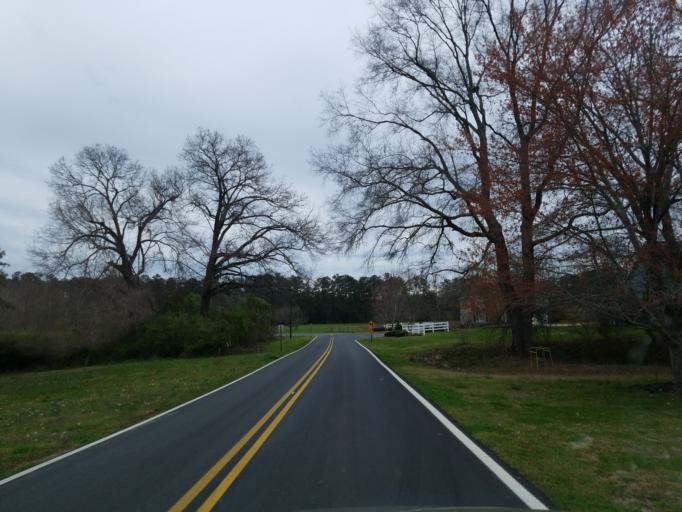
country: US
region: Georgia
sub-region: Bartow County
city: Cartersville
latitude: 34.2175
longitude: -84.7785
